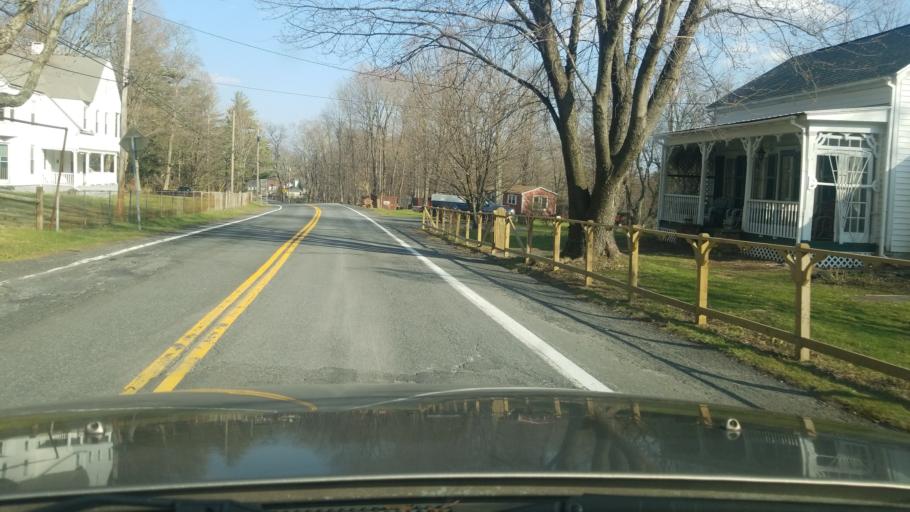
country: US
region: New York
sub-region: Greene County
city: Palenville
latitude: 42.1761
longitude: -74.0304
